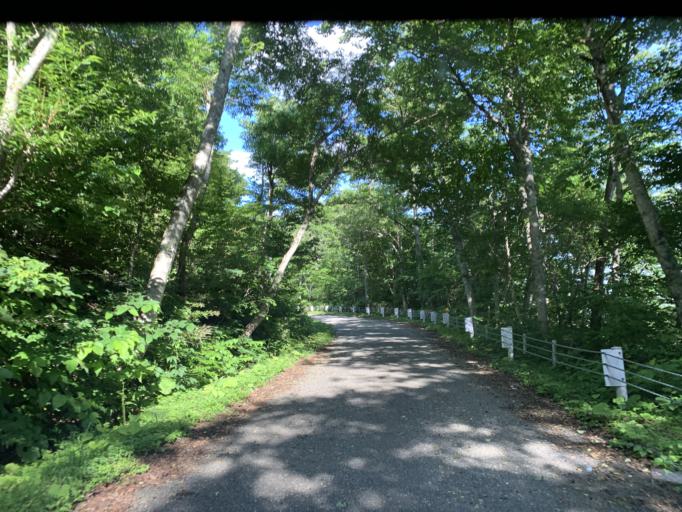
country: JP
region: Iwate
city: Ichinoseki
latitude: 38.9177
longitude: 140.8182
